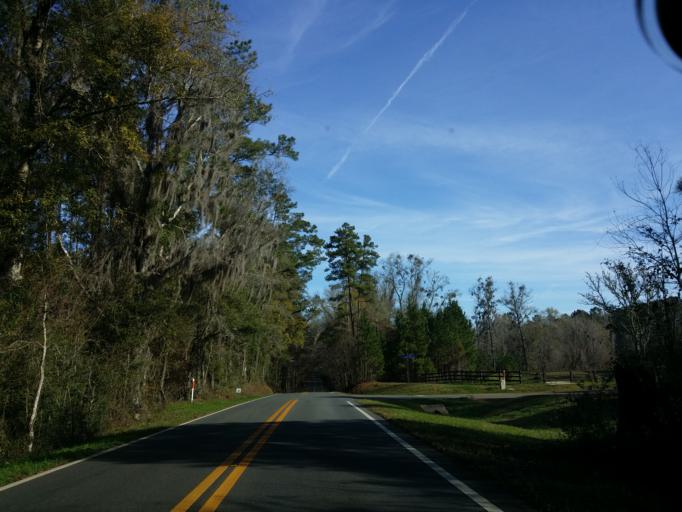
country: US
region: Florida
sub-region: Leon County
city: Woodville
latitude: 30.3844
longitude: -84.1553
